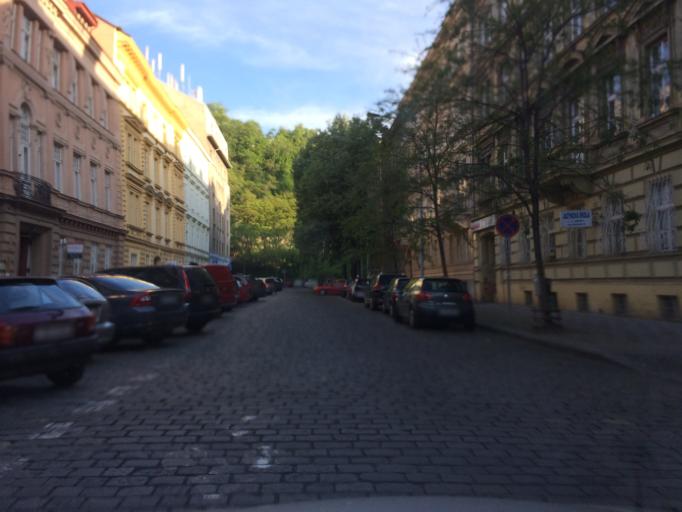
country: CZ
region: Praha
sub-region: Praha 8
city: Karlin
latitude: 50.0905
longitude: 14.4457
